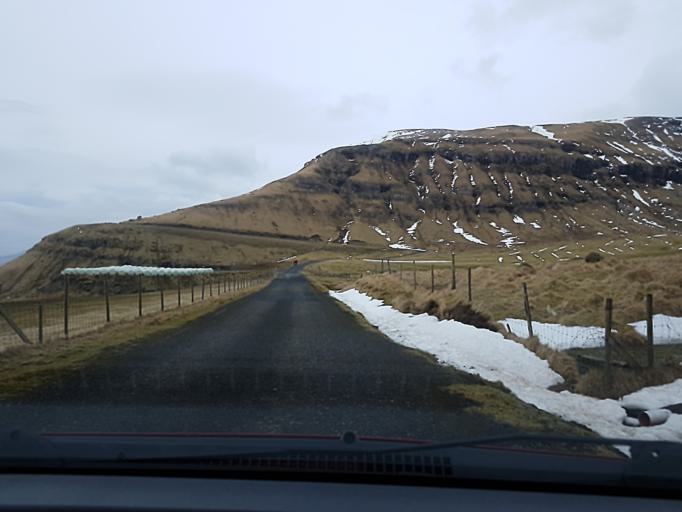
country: FO
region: Streymoy
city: Hoyvik
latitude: 61.9964
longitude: -6.8875
